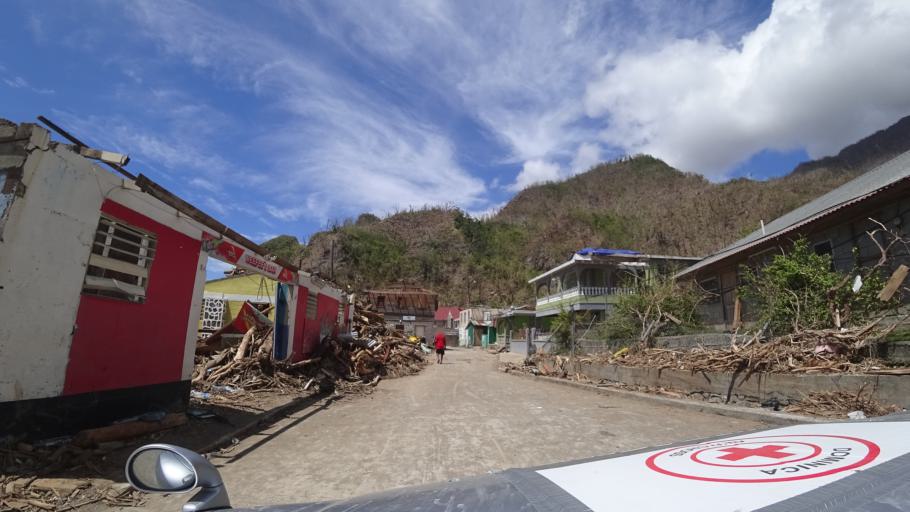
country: DM
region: Saint Mark
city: Soufriere
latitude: 15.2322
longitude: -61.3611
